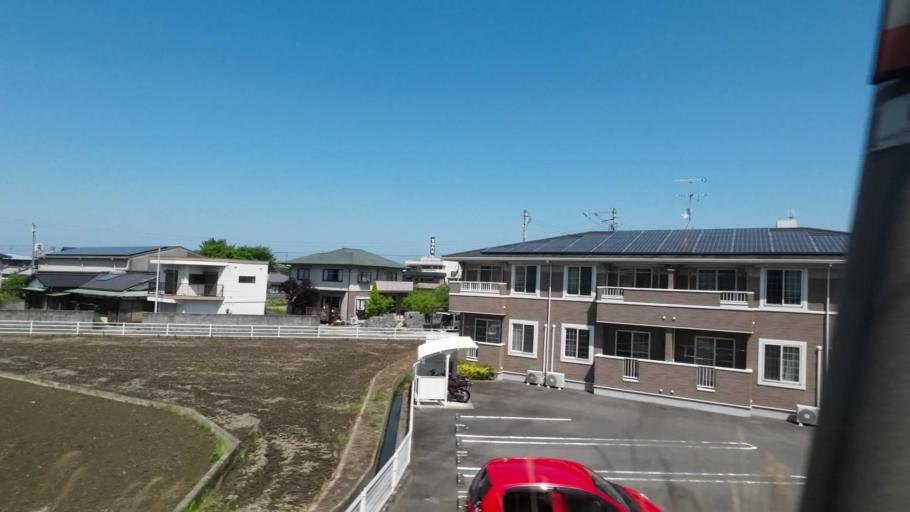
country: JP
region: Ehime
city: Niihama
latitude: 33.9681
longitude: 133.3197
